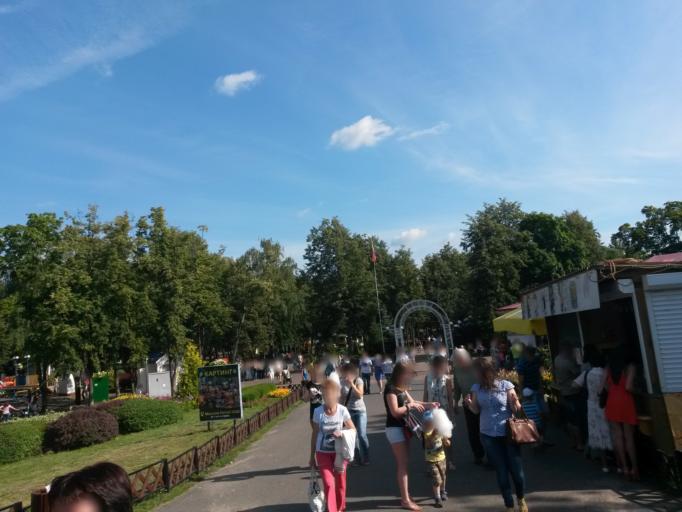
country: RU
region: Jaroslavl
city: Yaroslavl
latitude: 57.6199
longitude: 39.8986
